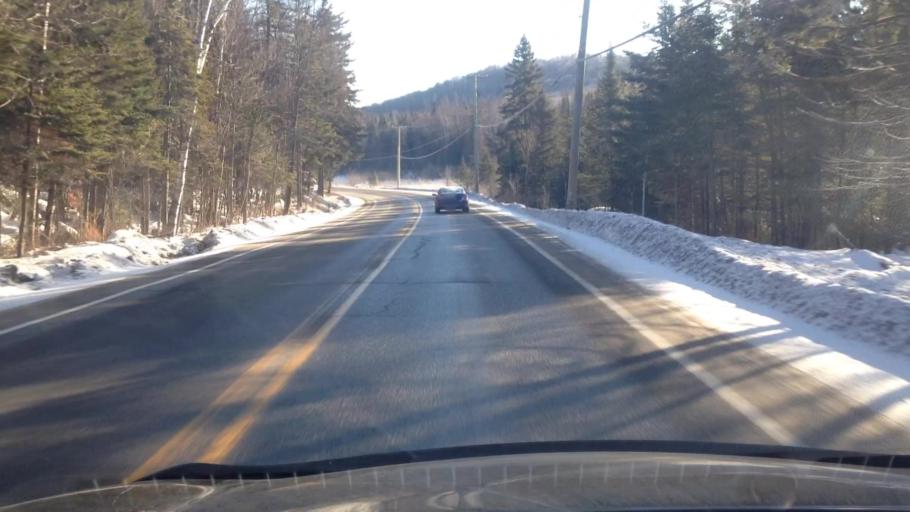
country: CA
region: Quebec
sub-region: Laurentides
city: Saint-Sauveur
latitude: 45.9089
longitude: -74.2851
